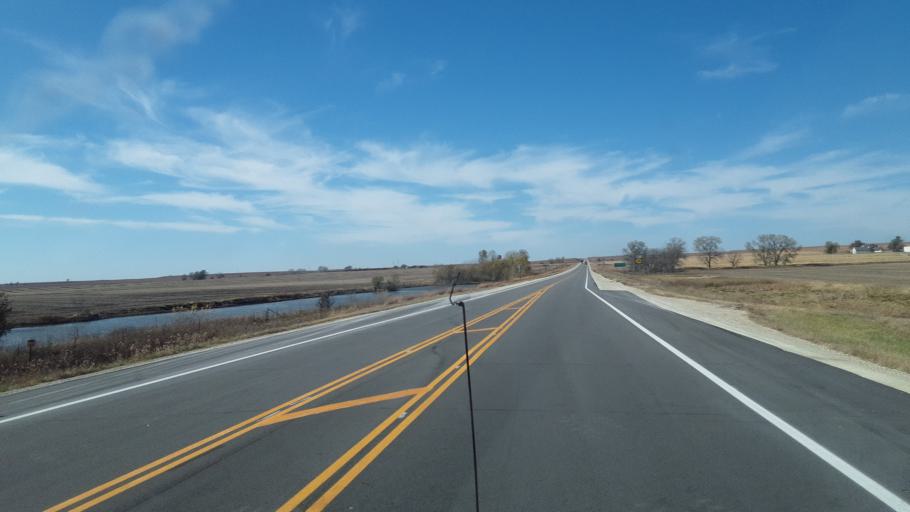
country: US
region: Kansas
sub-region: Chase County
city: Cottonwood Falls
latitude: 38.3627
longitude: -96.6621
